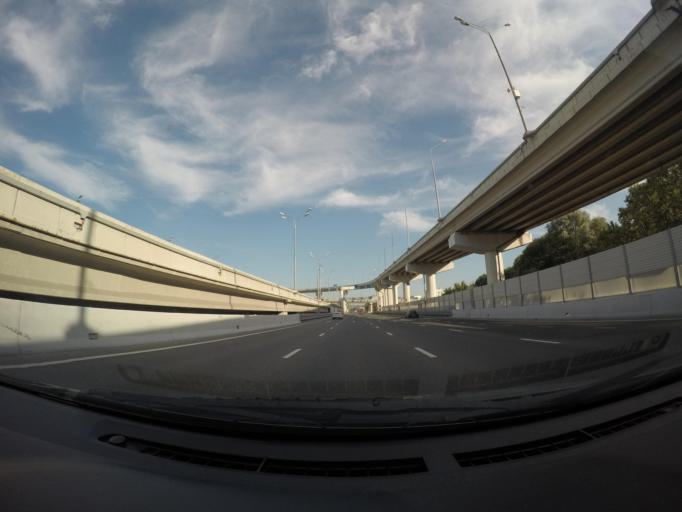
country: RU
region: Moscow
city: Novokhovrino
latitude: 55.8684
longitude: 37.5092
